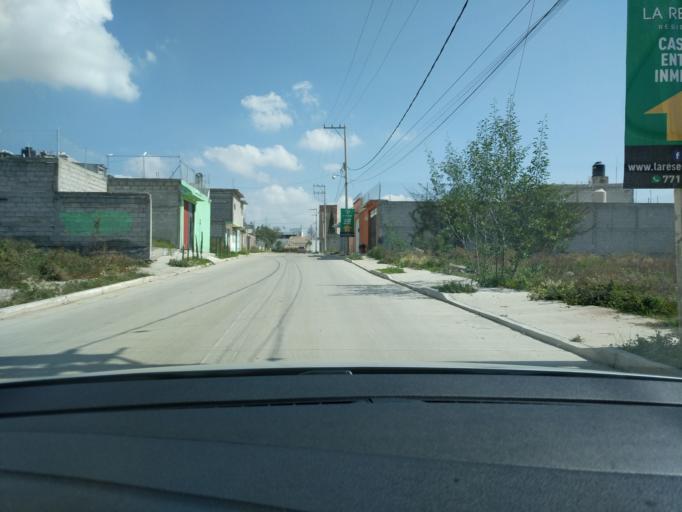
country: MX
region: Hidalgo
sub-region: Zempoala
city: El Mirador
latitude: 20.0250
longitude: -98.8131
